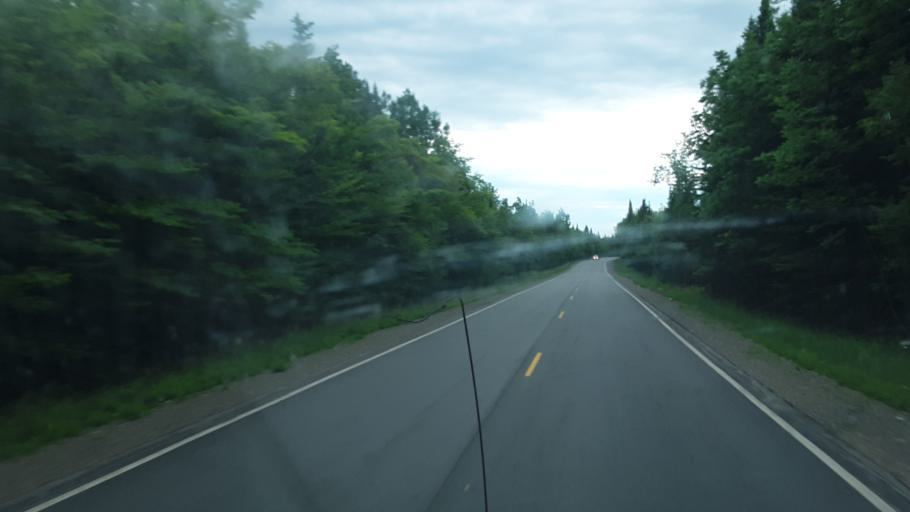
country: US
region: Maine
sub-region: Penobscot County
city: Medway
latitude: 45.7485
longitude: -68.3100
